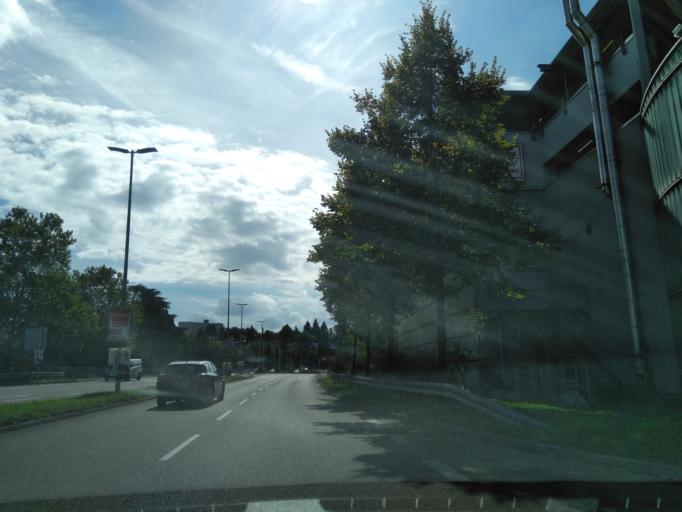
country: DE
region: Baden-Wuerttemberg
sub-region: Regierungsbezirk Stuttgart
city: Bietigheim-Bissingen
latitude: 48.9611
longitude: 9.1318
